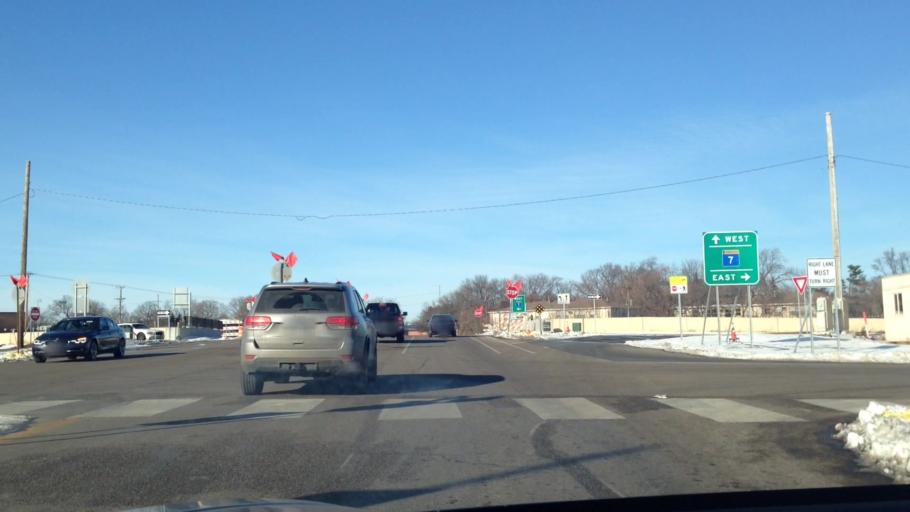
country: US
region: Minnesota
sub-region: Hennepin County
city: Saint Louis Park
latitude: 44.9385
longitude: -93.3557
